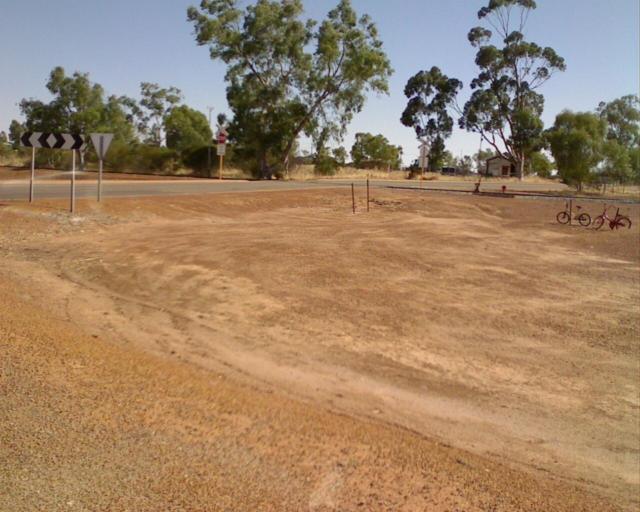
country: AU
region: Western Australia
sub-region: Wongan-Ballidu
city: Wongan Hills
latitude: -30.5956
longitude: 116.7664
